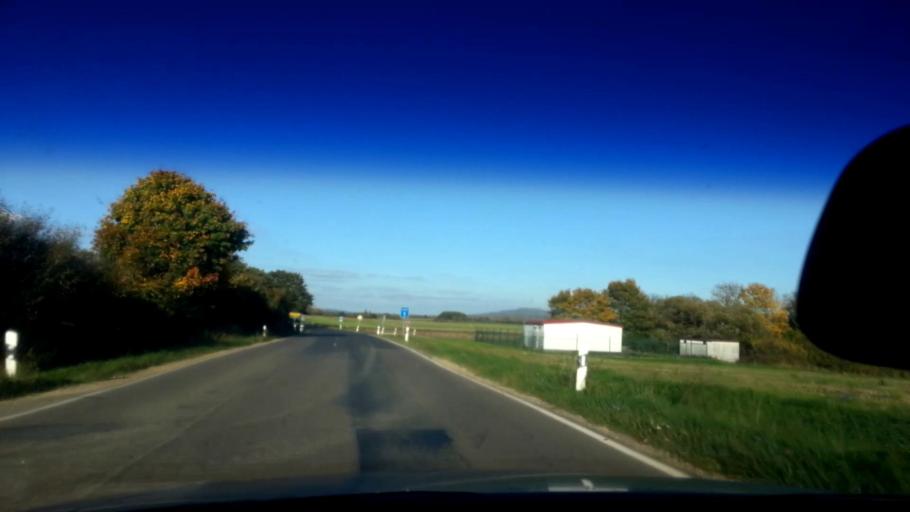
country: DE
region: Bavaria
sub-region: Upper Franconia
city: Rattelsdorf
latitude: 50.0242
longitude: 10.9062
